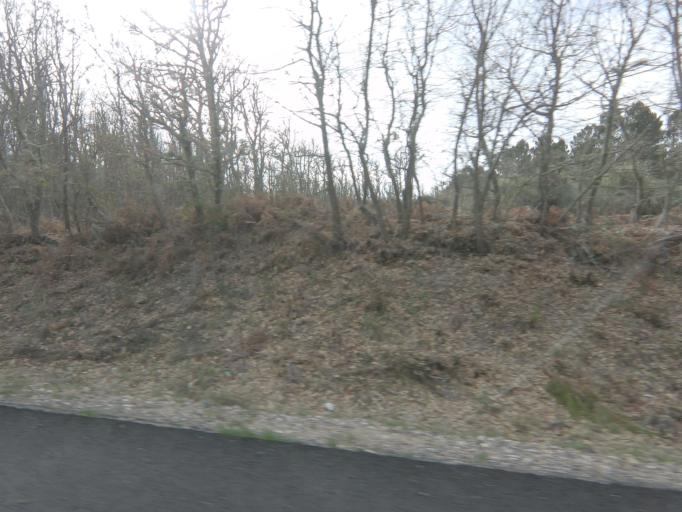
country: ES
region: Castille and Leon
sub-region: Provincia de Salamanca
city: Penaparda
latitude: 40.3056
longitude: -6.6513
